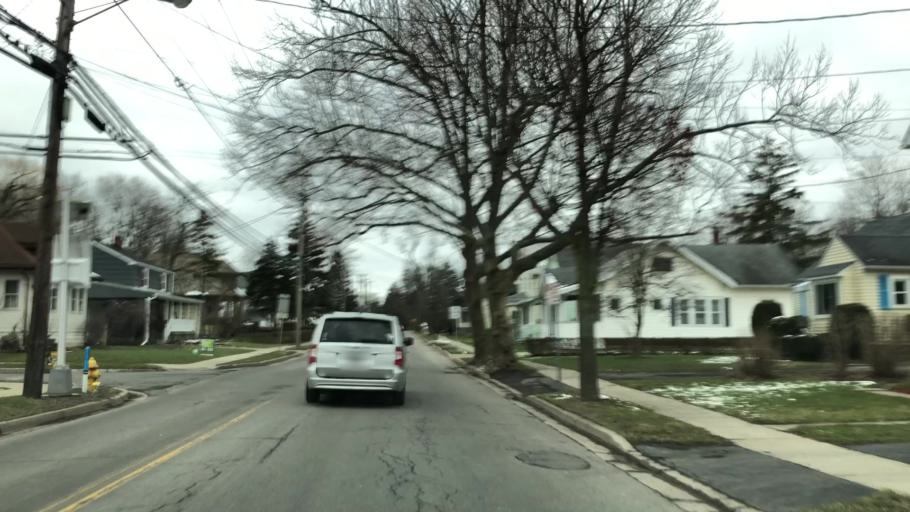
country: US
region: New York
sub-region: Erie County
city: Lancaster
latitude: 42.8954
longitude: -78.6755
